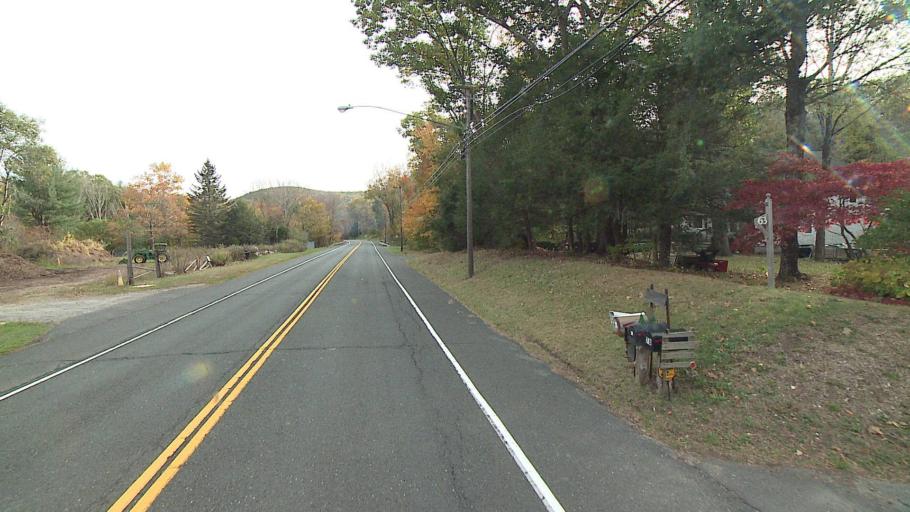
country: US
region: Connecticut
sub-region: Litchfield County
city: Winchester Center
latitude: 41.9487
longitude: -73.1143
